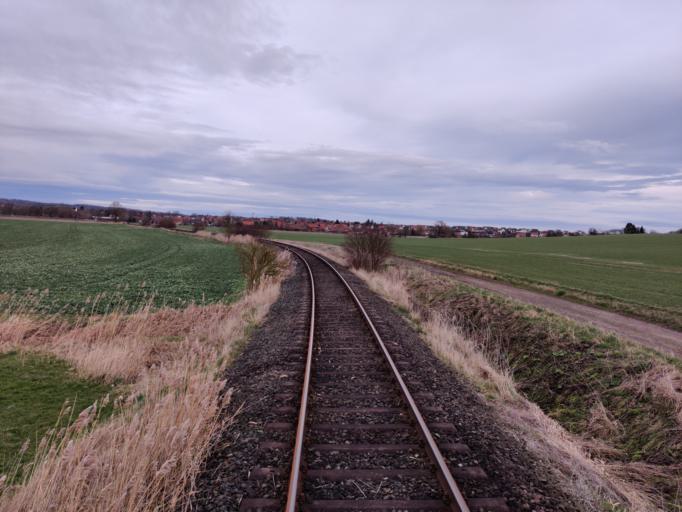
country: DE
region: Lower Saxony
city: Holle
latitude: 52.0765
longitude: 10.1532
